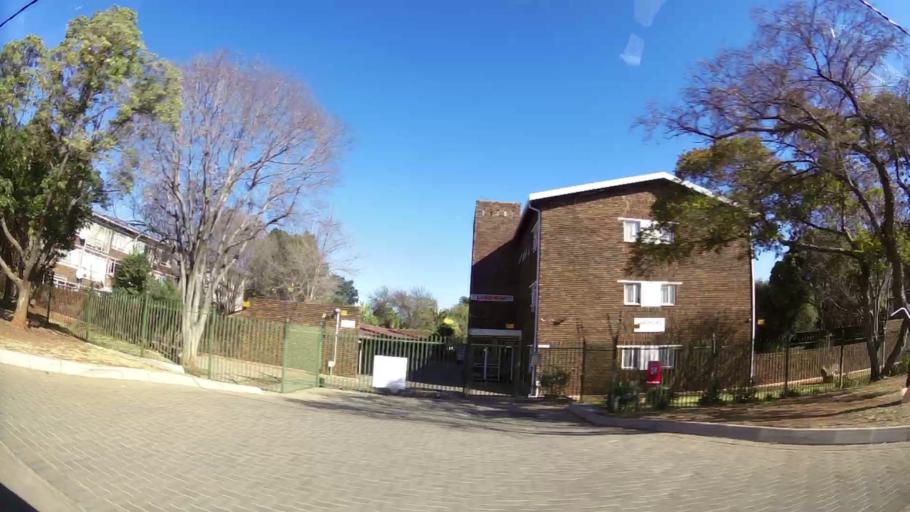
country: ZA
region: Gauteng
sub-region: City of Tshwane Metropolitan Municipality
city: Centurion
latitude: -25.8569
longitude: 28.2150
